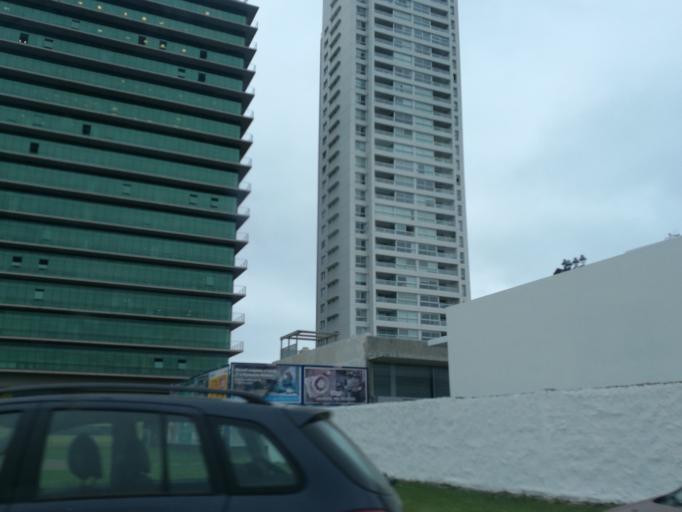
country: AR
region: Santa Fe
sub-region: Departamento de Rosario
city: Rosario
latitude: -32.9257
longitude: -60.6608
